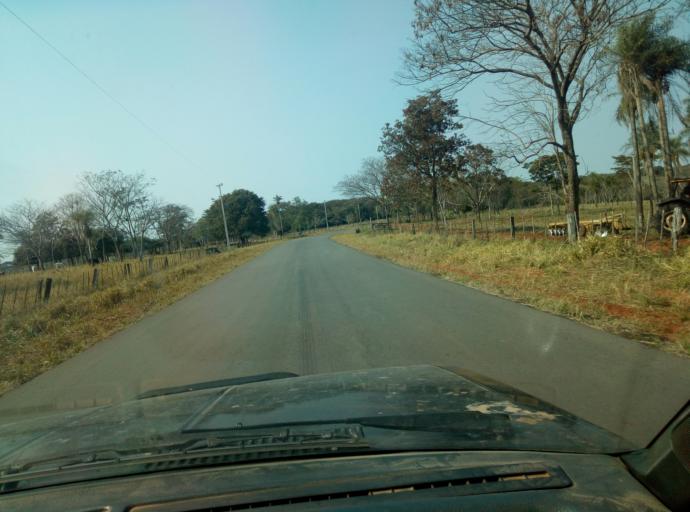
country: PY
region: Caaguazu
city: Carayao
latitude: -25.1938
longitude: -56.3104
